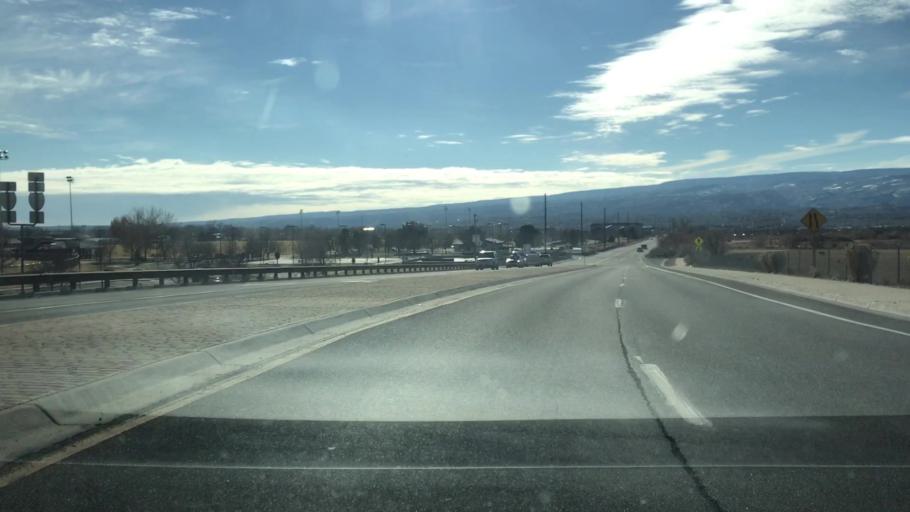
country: US
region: Colorado
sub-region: Mesa County
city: Redlands
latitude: 39.1129
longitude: -108.6084
